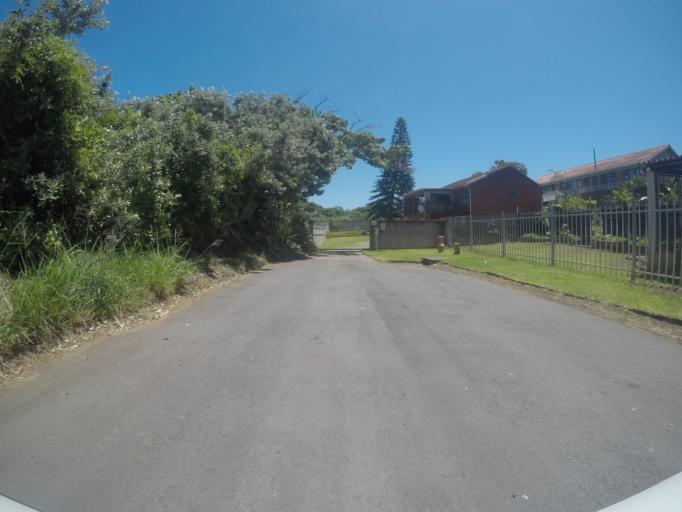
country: ZA
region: Eastern Cape
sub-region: Buffalo City Metropolitan Municipality
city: East London
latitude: -32.9570
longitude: 27.9962
